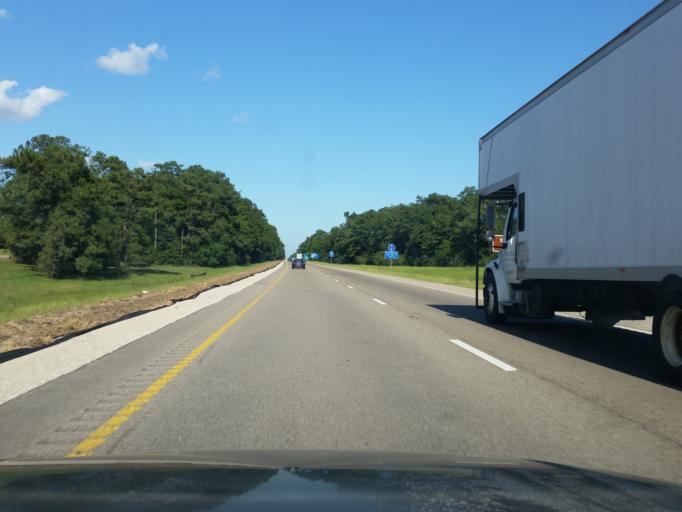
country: US
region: Mississippi
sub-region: Hancock County
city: Pearlington
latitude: 30.3072
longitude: -89.6249
